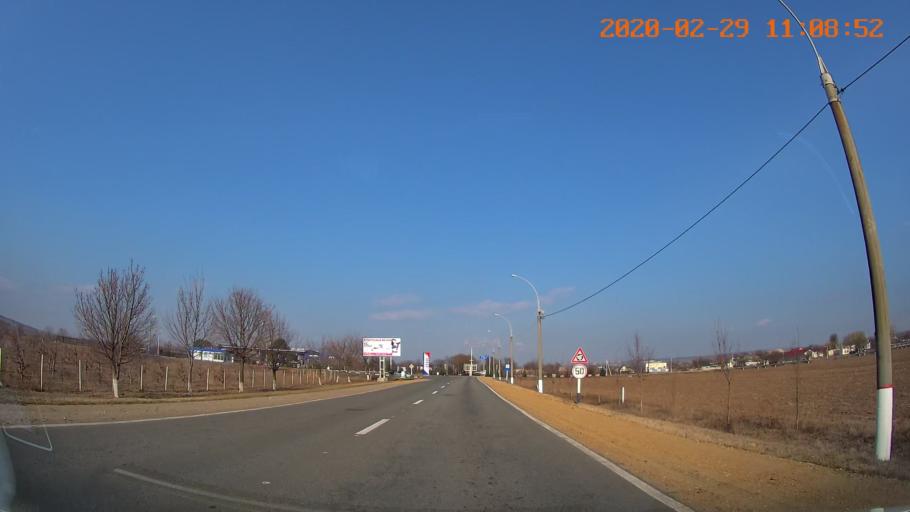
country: MD
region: Criuleni
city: Criuleni
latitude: 47.2375
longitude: 29.1727
